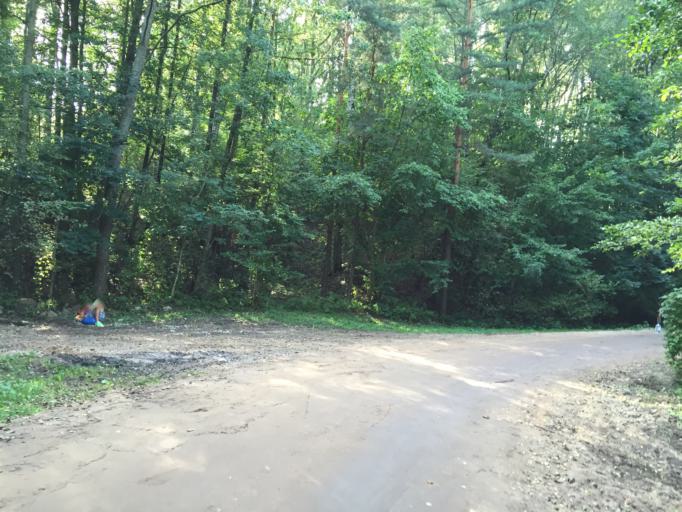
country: LT
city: Zarasai
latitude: 55.7865
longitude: 25.9578
